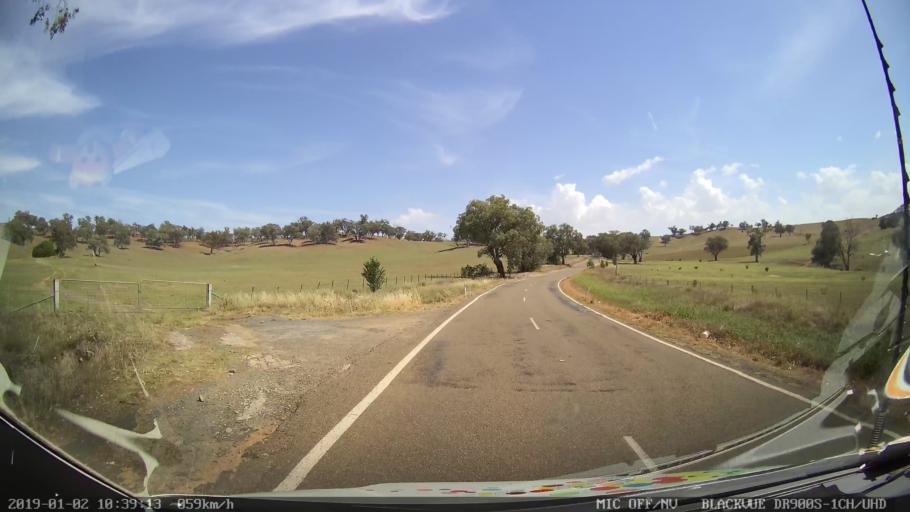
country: AU
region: New South Wales
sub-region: Gundagai
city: Gundagai
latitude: -34.8128
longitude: 148.3196
